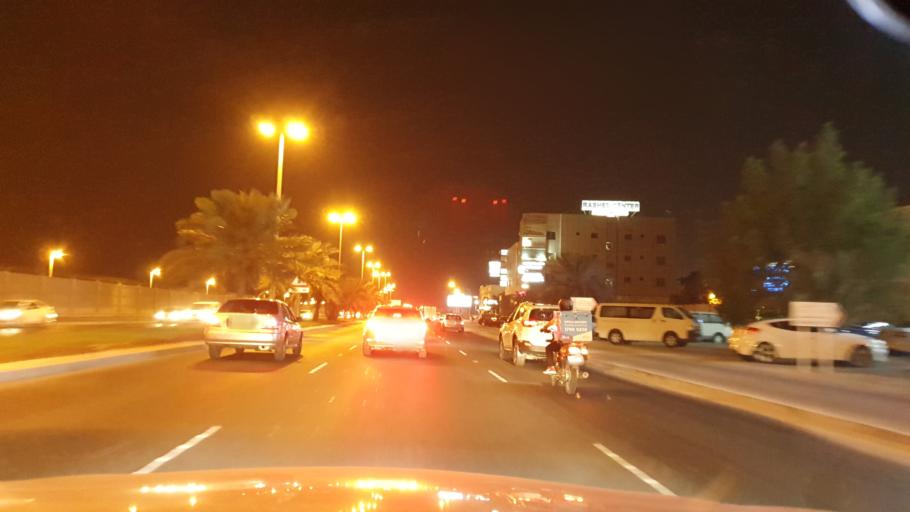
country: BH
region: Muharraq
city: Al Hadd
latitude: 26.2584
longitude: 50.6470
